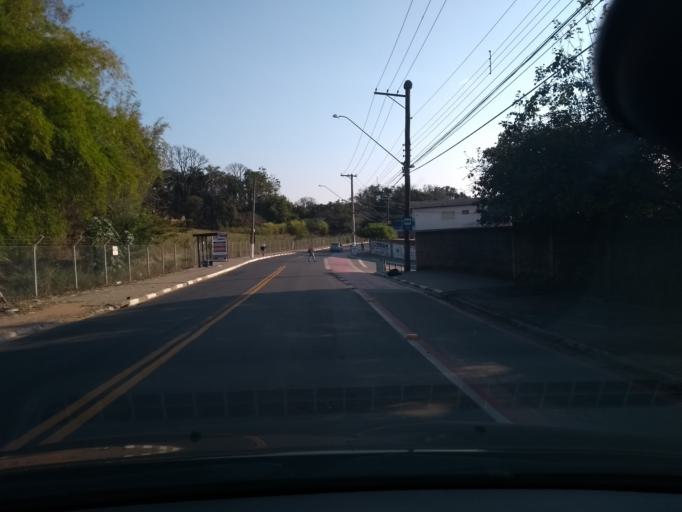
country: BR
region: Sao Paulo
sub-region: Itupeva
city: Itupeva
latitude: -23.1505
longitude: -47.0458
